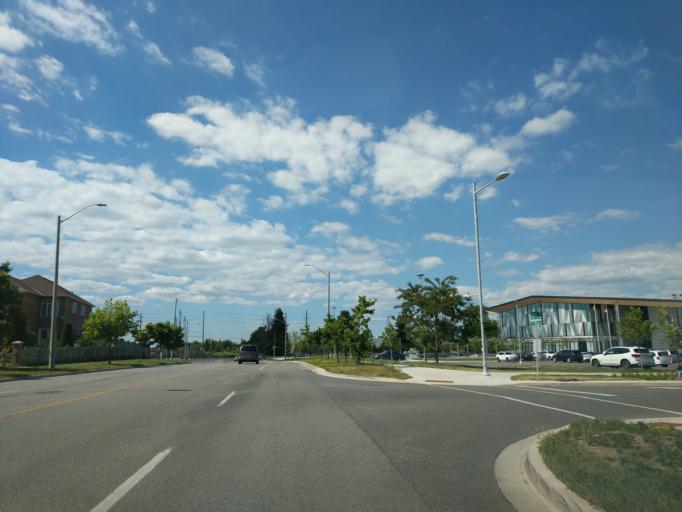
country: CA
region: Ontario
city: Markham
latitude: 43.8506
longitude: -79.2673
